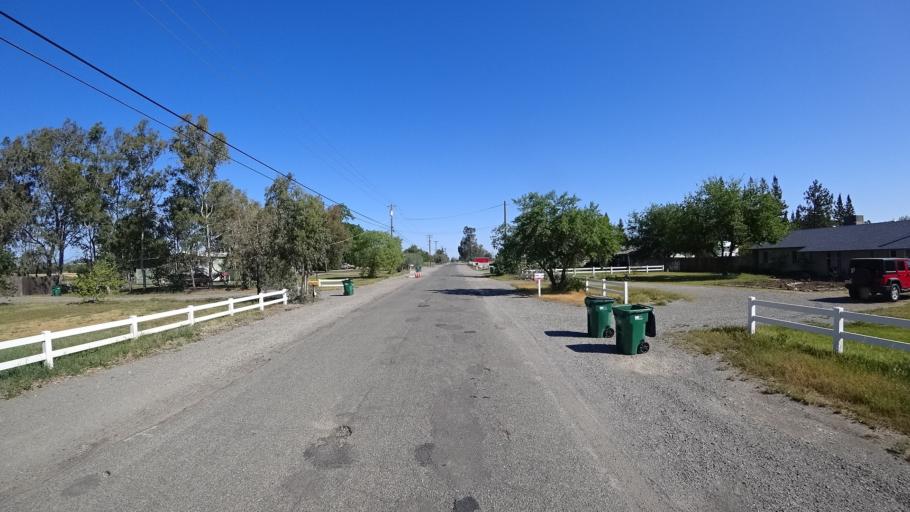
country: US
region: California
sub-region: Glenn County
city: Orland
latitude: 39.7273
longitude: -122.1689
